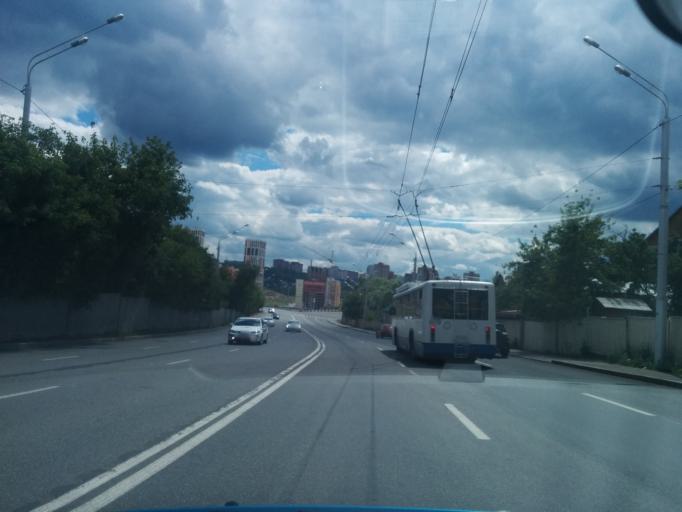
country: RU
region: Bashkortostan
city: Ufa
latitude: 54.7232
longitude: 55.9754
